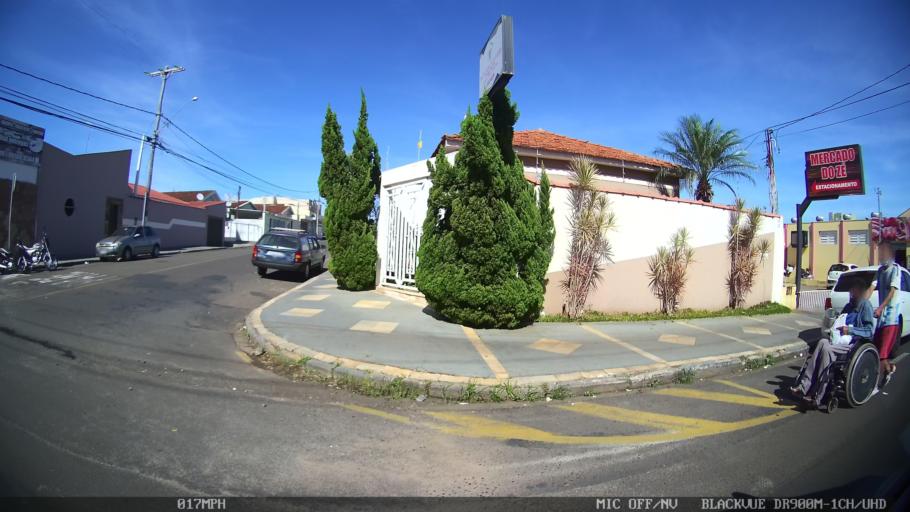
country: BR
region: Sao Paulo
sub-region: Franca
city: Franca
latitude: -20.5423
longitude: -47.3852
